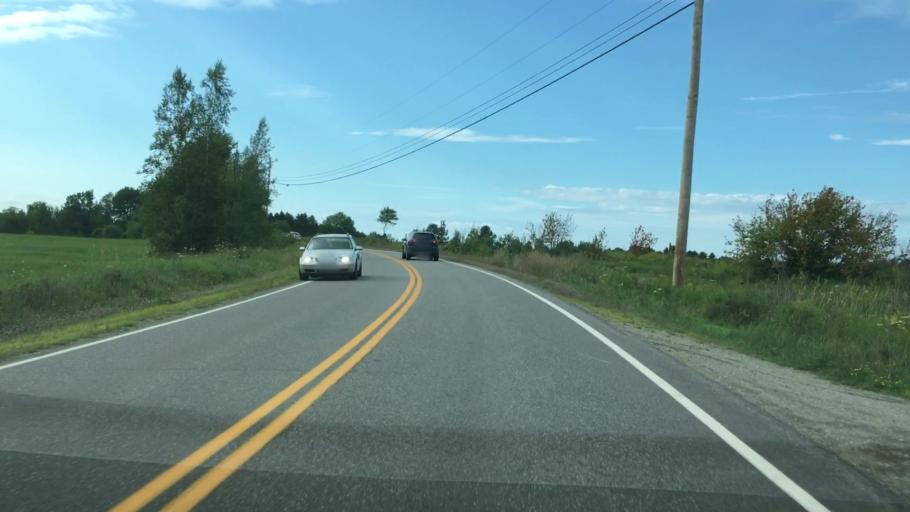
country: US
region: Maine
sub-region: Waldo County
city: Belfast
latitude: 44.3756
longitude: -69.0316
